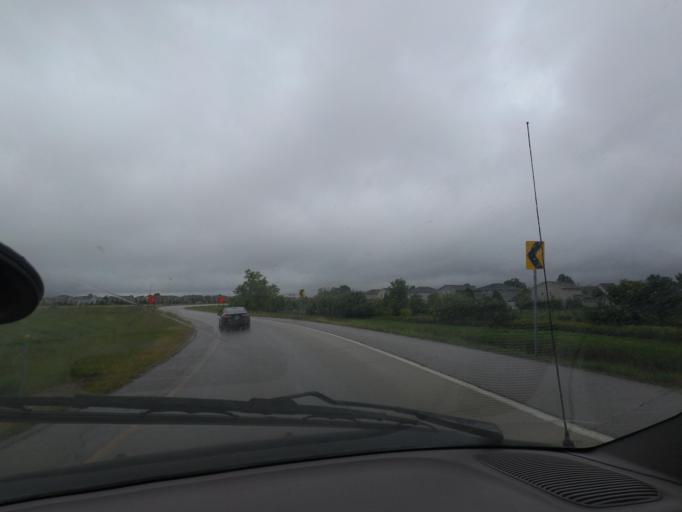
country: US
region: Illinois
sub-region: Champaign County
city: Champaign
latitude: 40.1212
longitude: -88.3031
